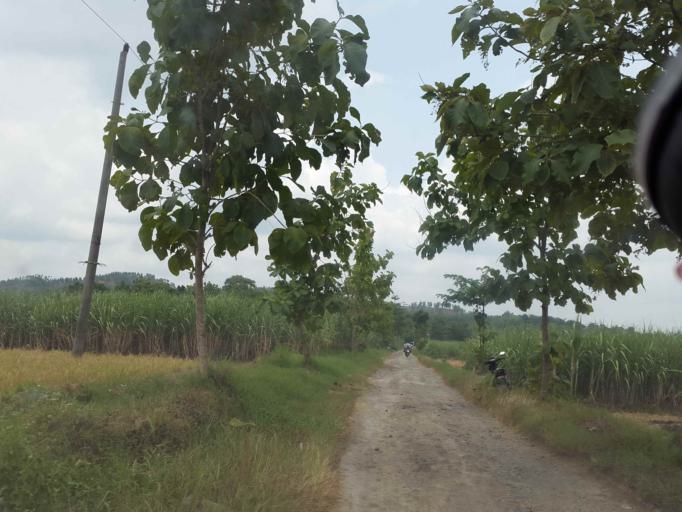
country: ID
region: Central Java
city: Pemalang
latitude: -6.9498
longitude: 109.2899
